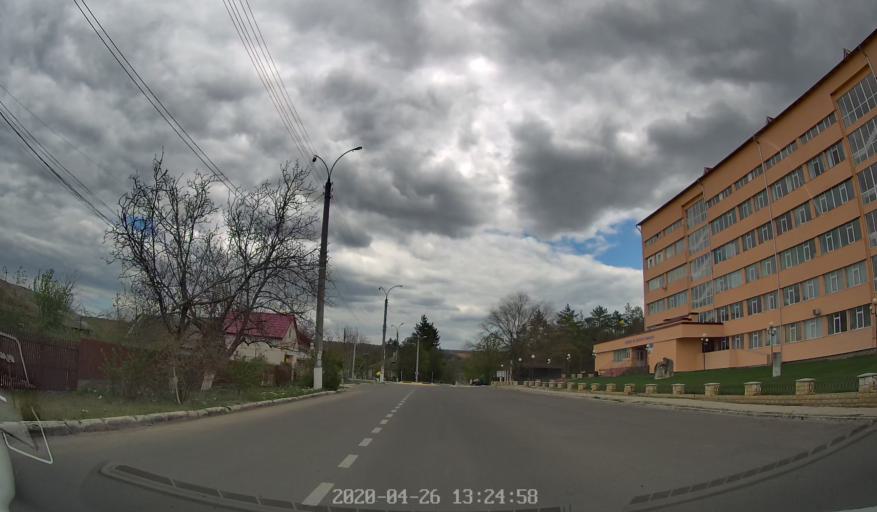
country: MD
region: Criuleni
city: Criuleni
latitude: 47.2066
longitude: 29.1661
